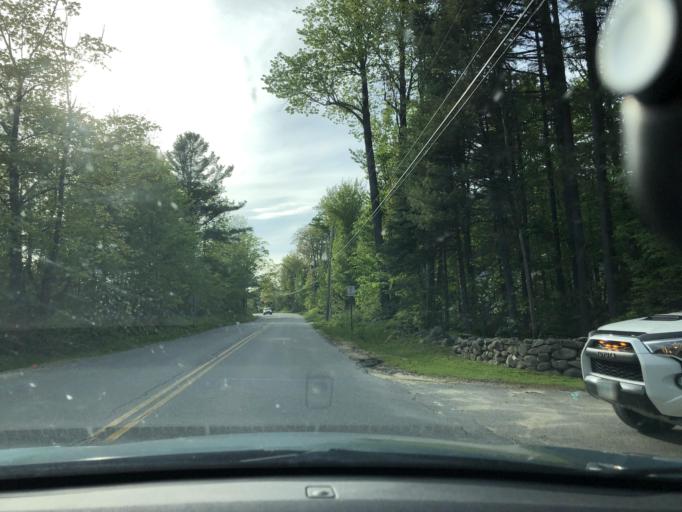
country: US
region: New Hampshire
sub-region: Merrimack County
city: New London
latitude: 43.4137
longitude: -71.9717
